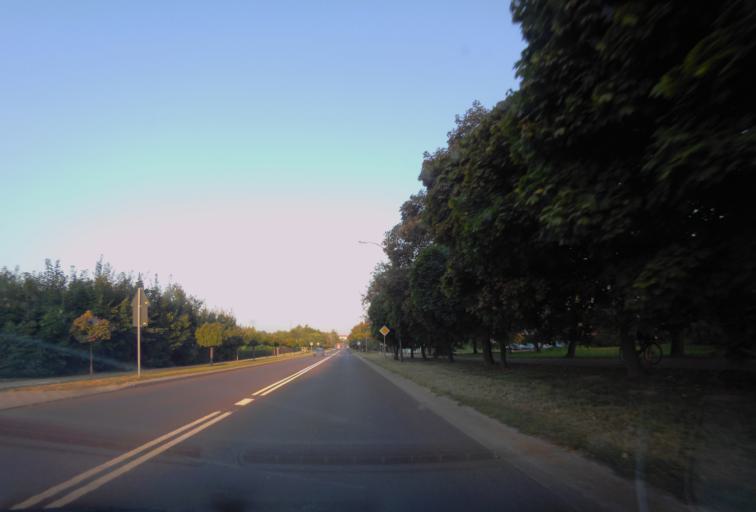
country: PL
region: Lublin Voivodeship
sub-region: Powiat janowski
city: Janow Lubelski
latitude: 50.7010
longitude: 22.4319
